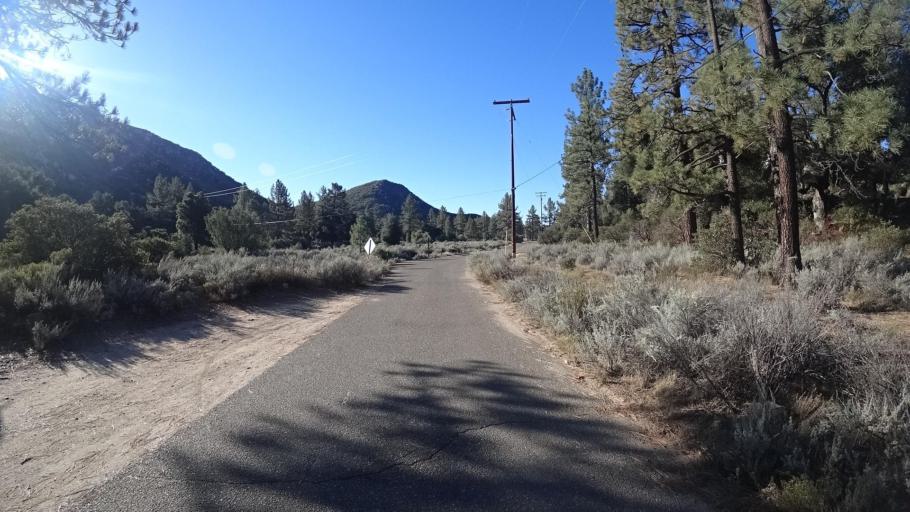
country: US
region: California
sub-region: San Diego County
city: Pine Valley
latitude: 32.8546
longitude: -116.5228
